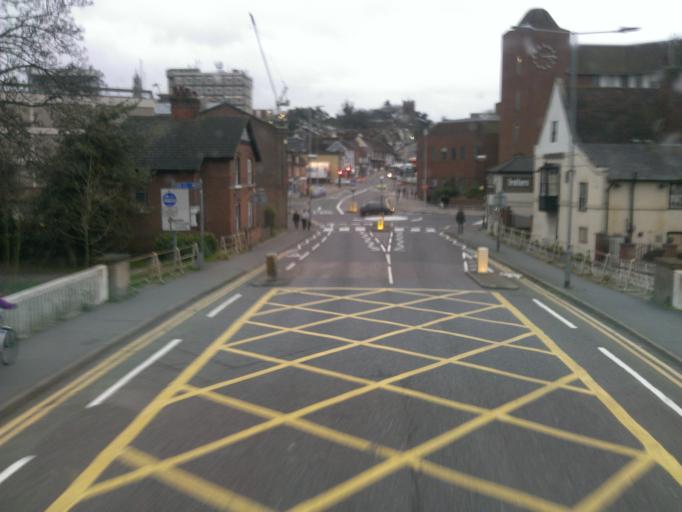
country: GB
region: England
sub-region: Essex
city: Colchester
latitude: 51.8939
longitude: 0.8961
